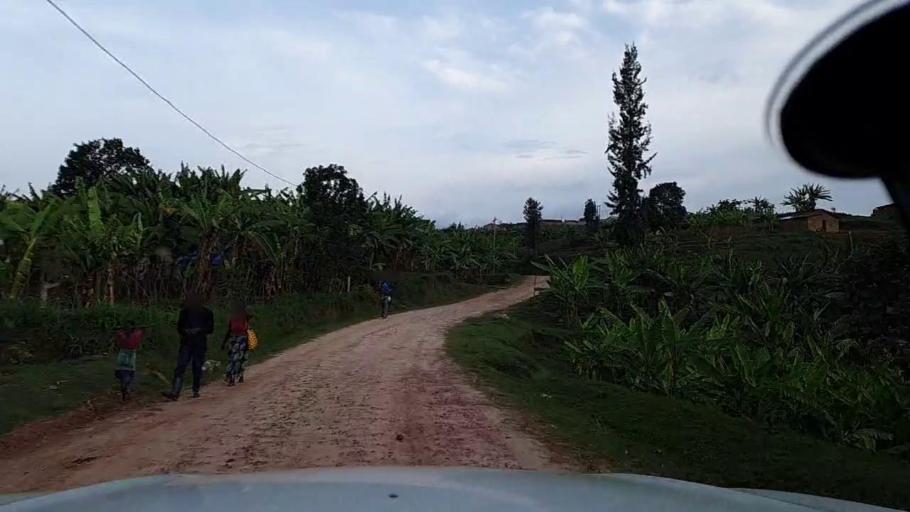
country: RW
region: Southern Province
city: Gitarama
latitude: -2.2095
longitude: 29.6065
